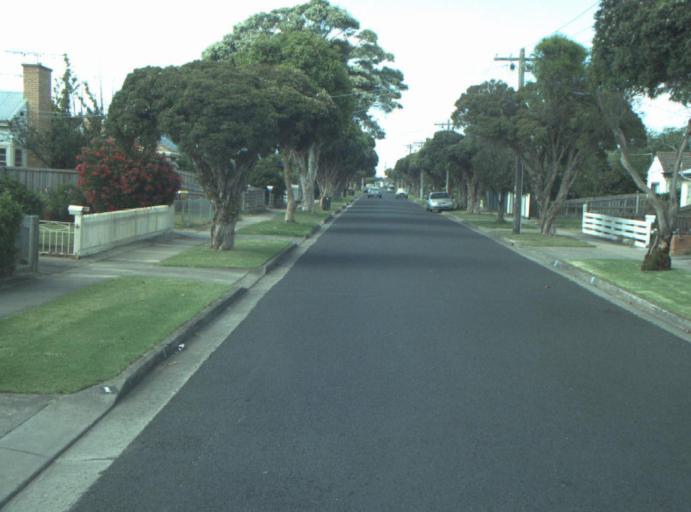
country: AU
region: Victoria
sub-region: Greater Geelong
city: Breakwater
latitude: -38.1750
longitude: 144.3359
